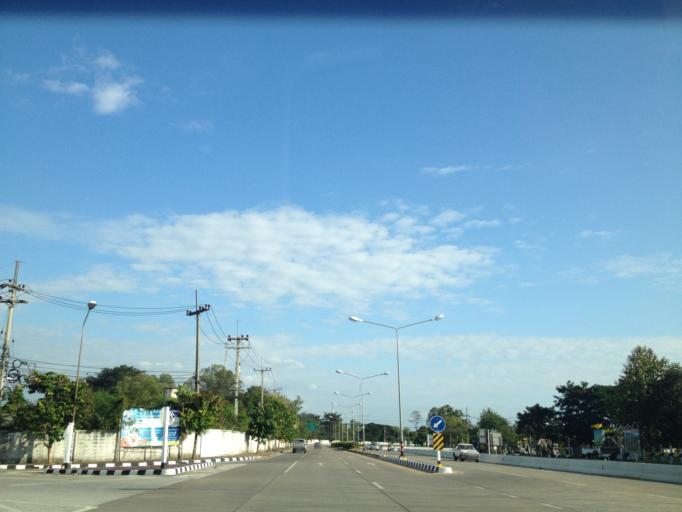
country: TH
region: Chiang Mai
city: Chiang Mai
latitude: 18.8436
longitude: 98.9627
